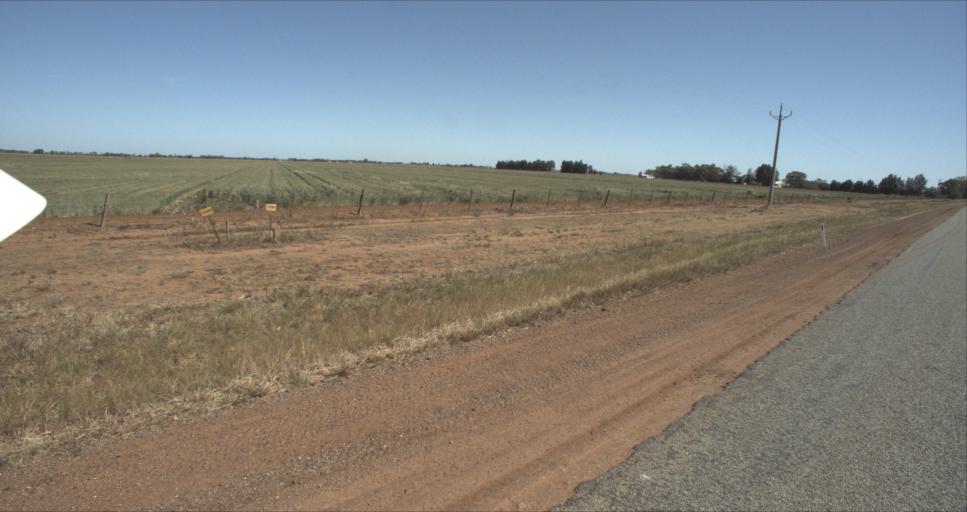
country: AU
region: New South Wales
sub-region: Leeton
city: Leeton
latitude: -34.5488
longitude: 146.3151
